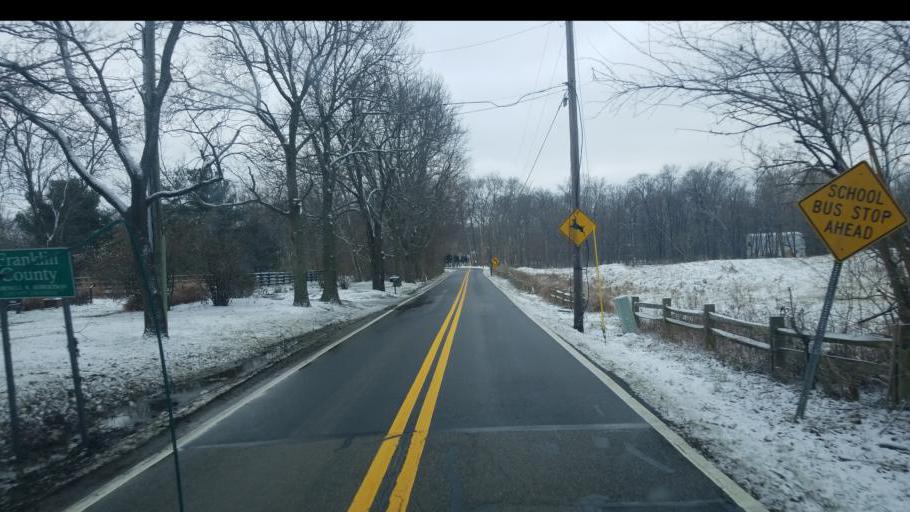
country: US
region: Ohio
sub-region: Franklin County
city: New Albany
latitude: 40.0449
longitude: -82.8368
